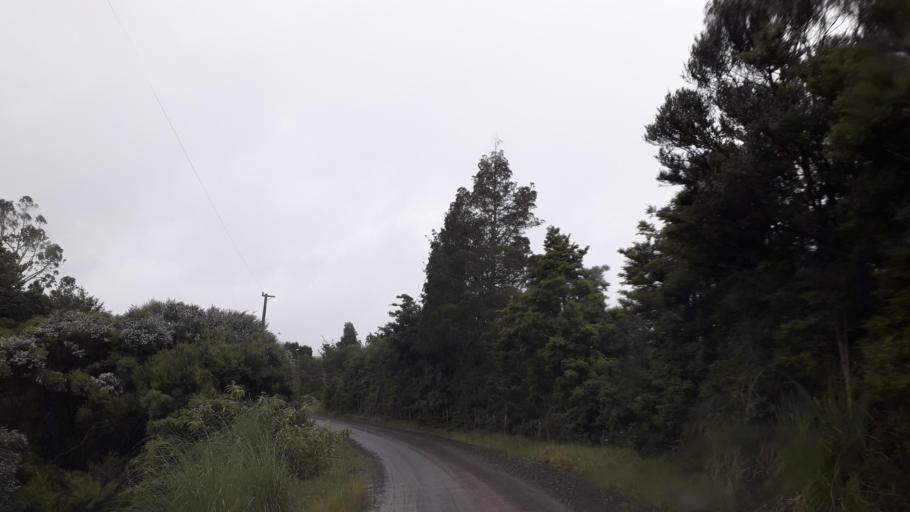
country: NZ
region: Northland
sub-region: Far North District
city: Kaitaia
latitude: -35.3803
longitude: 173.4099
